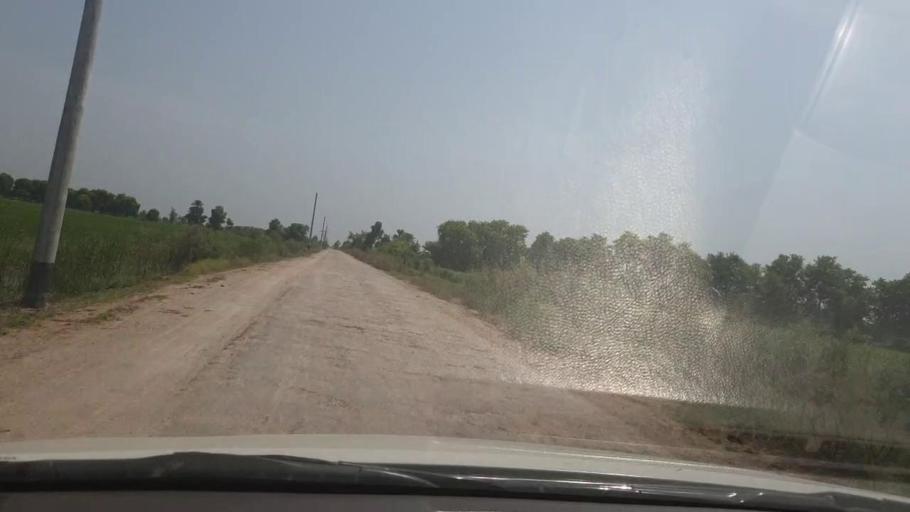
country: PK
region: Sindh
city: Garhi Yasin
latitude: 27.9766
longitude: 68.5031
